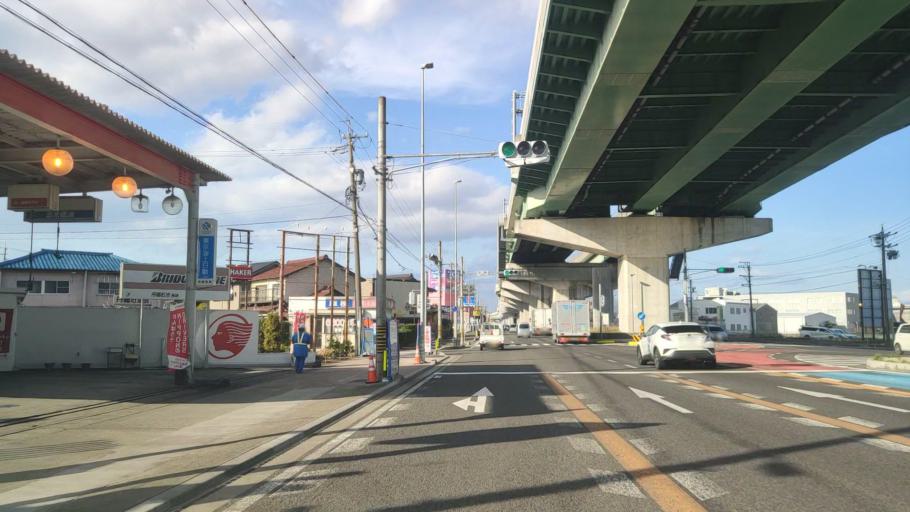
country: JP
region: Aichi
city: Ichinomiya
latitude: 35.2780
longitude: 136.8298
